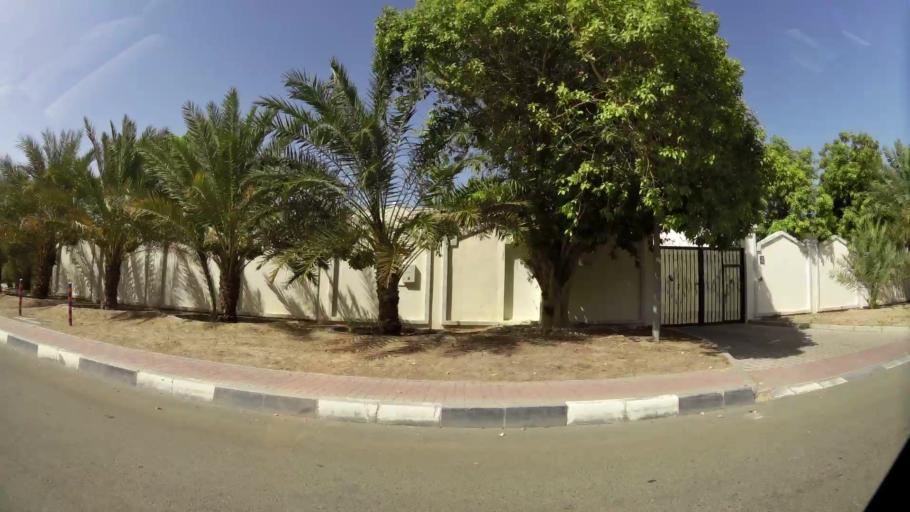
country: OM
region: Al Buraimi
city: Al Buraymi
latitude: 24.3008
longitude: 55.7992
